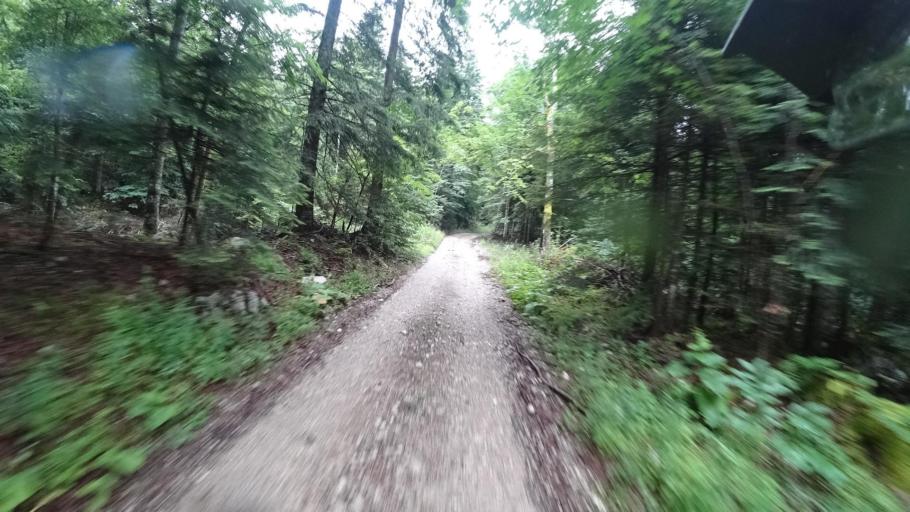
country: HR
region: Karlovacka
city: Plaski
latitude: 44.9292
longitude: 15.4286
